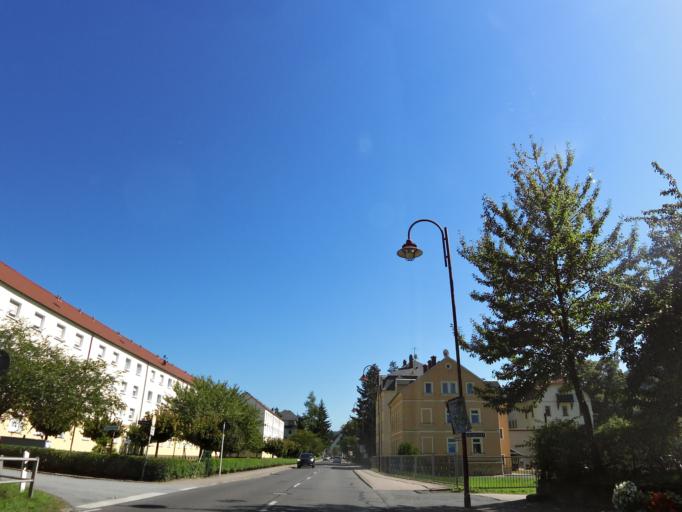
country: DE
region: Saxony
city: Bad Schandau
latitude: 50.9199
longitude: 14.1459
